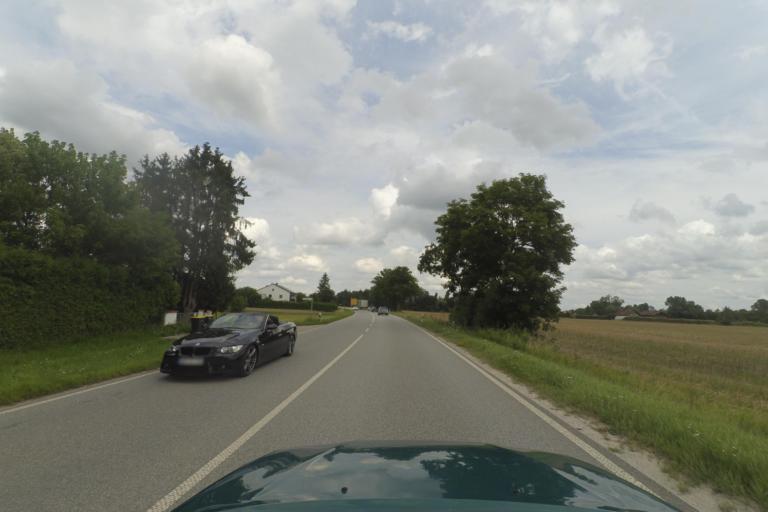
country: DE
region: Bavaria
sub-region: Lower Bavaria
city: Mamming
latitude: 48.6650
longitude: 12.5852
